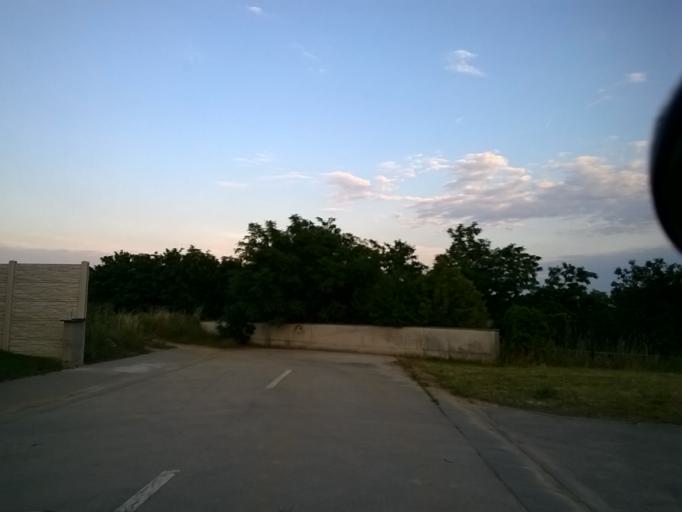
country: SK
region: Trnavsky
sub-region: Okres Senica
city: Senica
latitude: 48.6870
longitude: 17.3822
